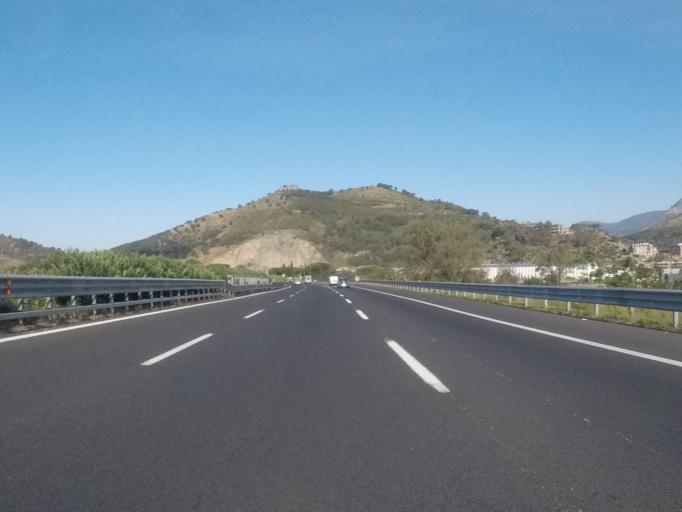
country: IT
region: Campania
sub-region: Provincia di Salerno
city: Casali-San Potito
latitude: 40.7693
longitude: 14.6727
